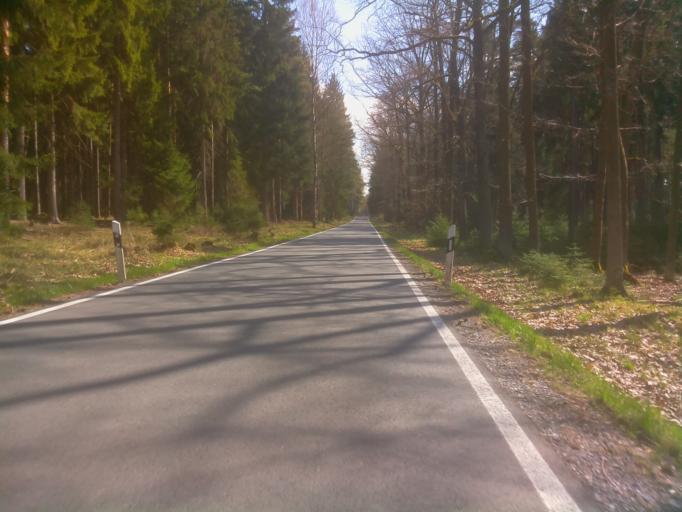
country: DE
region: Thuringia
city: Oberbodnitz
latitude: 50.7745
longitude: 11.6602
